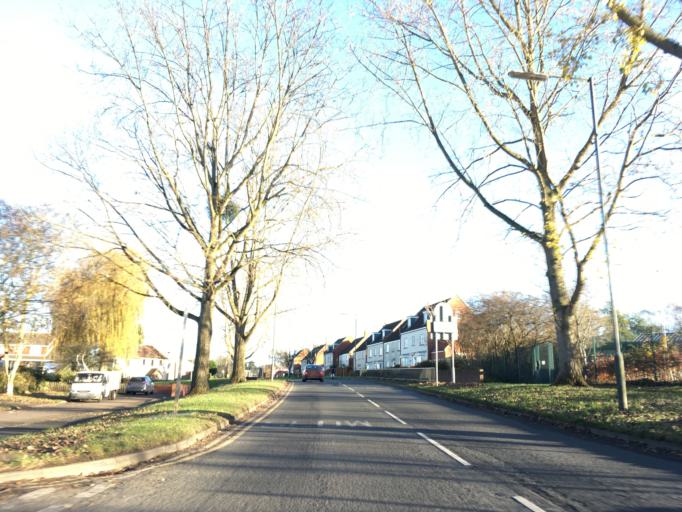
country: GB
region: England
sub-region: South Gloucestershire
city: Thornbury
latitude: 51.6073
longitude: -2.5204
